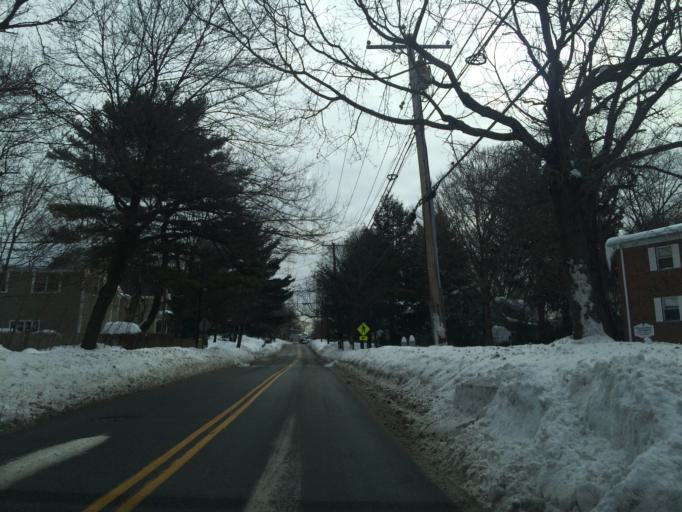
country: US
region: Massachusetts
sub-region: Norfolk County
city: Wellesley
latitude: 42.3280
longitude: -71.2621
